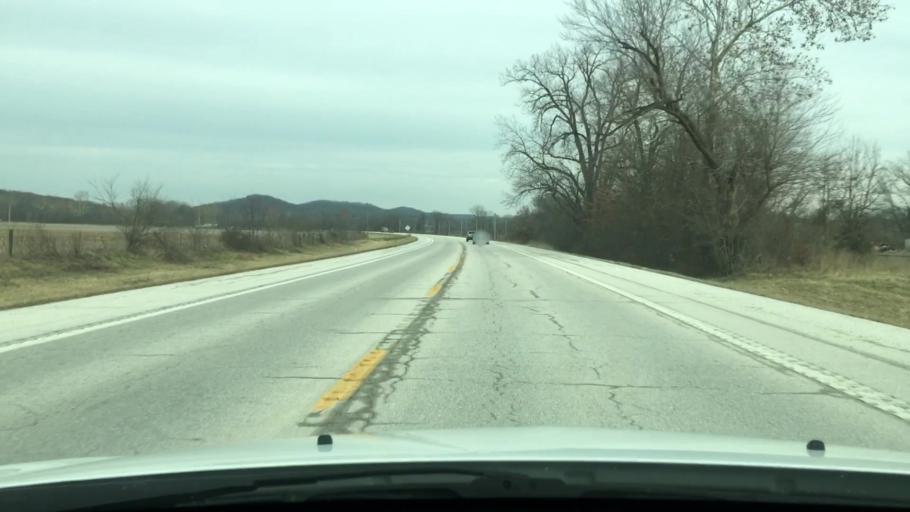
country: US
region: Missouri
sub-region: Pike County
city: Bowling Green
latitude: 39.3855
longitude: -91.1242
